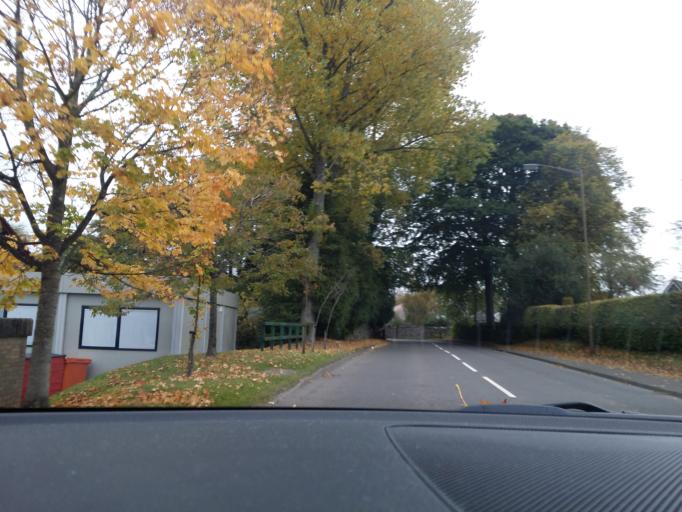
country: GB
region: Scotland
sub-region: Stirling
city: Stirling
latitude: 56.1073
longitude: -3.9541
